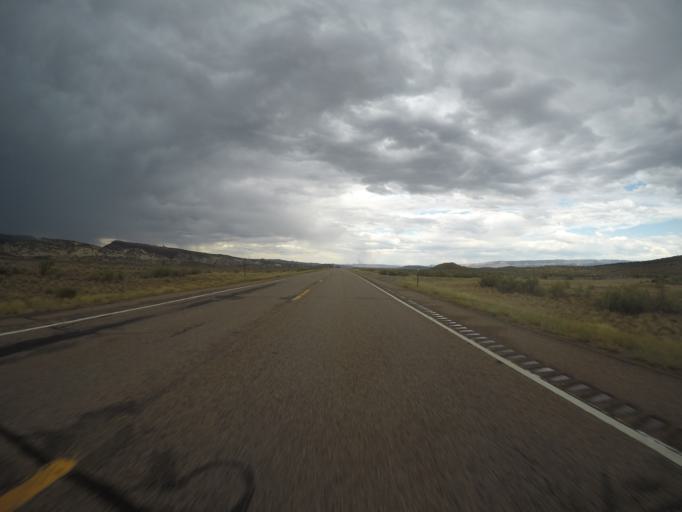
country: US
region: Colorado
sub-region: Rio Blanco County
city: Rangely
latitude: 40.2513
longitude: -108.8023
